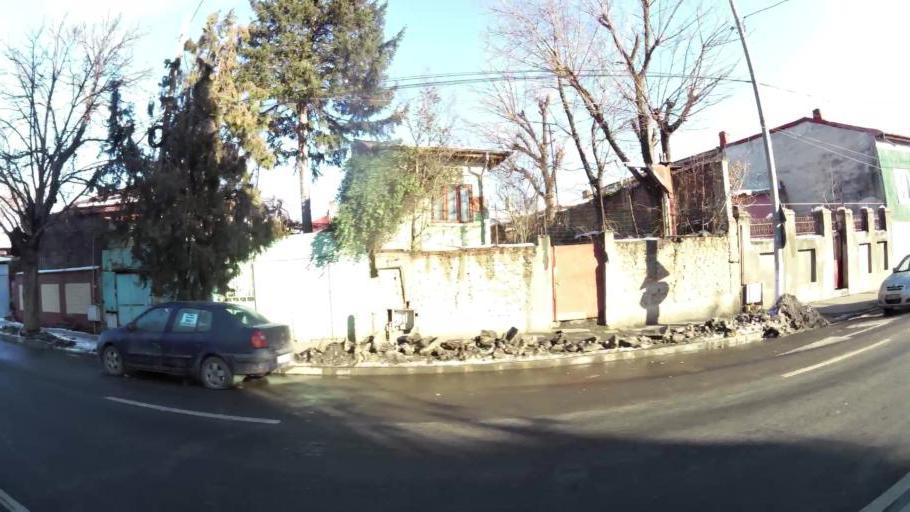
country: RO
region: Ilfov
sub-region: Comuna Fundeni-Dobroesti
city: Fundeni
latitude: 44.4720
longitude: 26.1415
